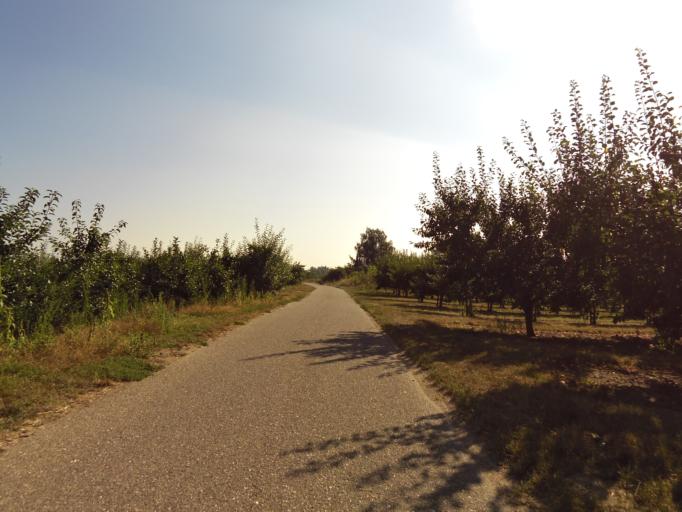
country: DE
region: Rheinland-Pfalz
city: Weisenheim am Sand
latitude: 49.5103
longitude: 8.2311
